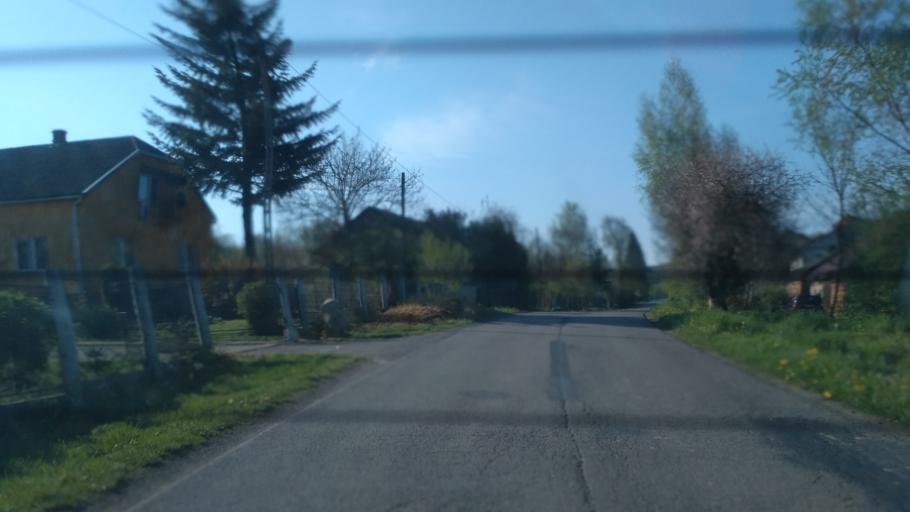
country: PL
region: Subcarpathian Voivodeship
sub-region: Powiat jaroslawski
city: Pruchnik
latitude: 49.8776
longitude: 22.5644
